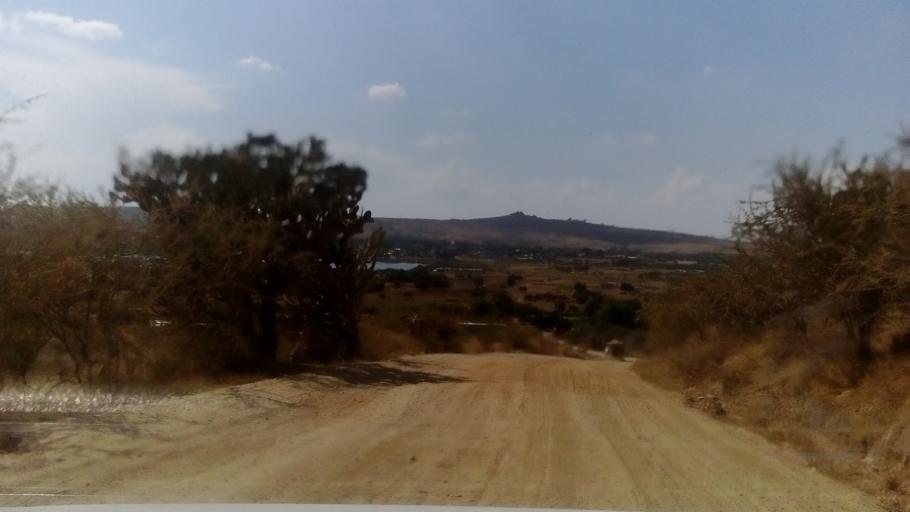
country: MX
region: Guanajuato
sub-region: Silao de la Victoria
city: Loma de Yerbabuena
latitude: 21.0685
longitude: -101.4571
